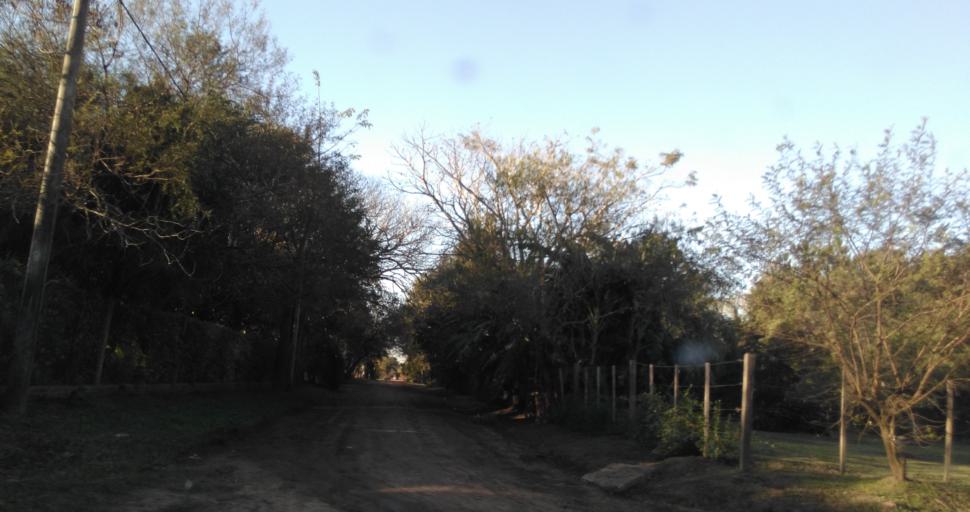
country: AR
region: Chaco
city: Colonia Benitez
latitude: -27.3303
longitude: -58.9574
